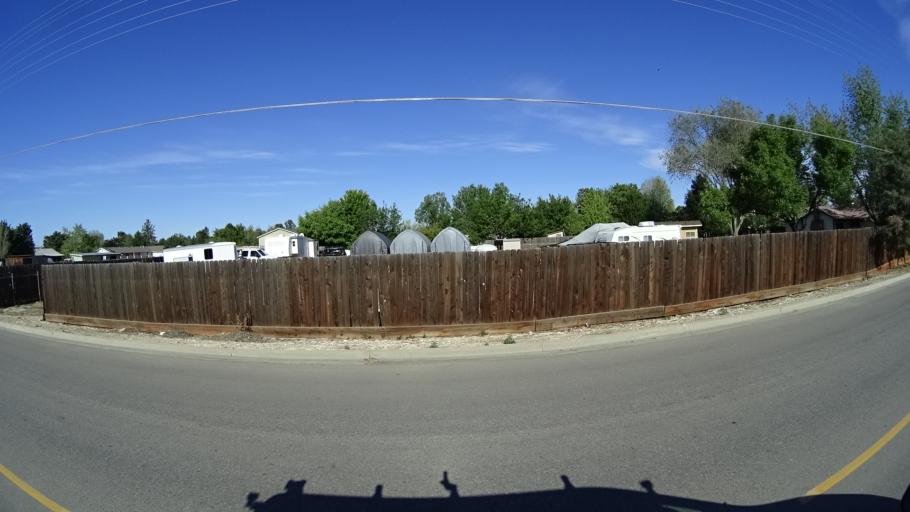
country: US
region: Idaho
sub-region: Ada County
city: Garden City
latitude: 43.5495
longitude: -116.2742
